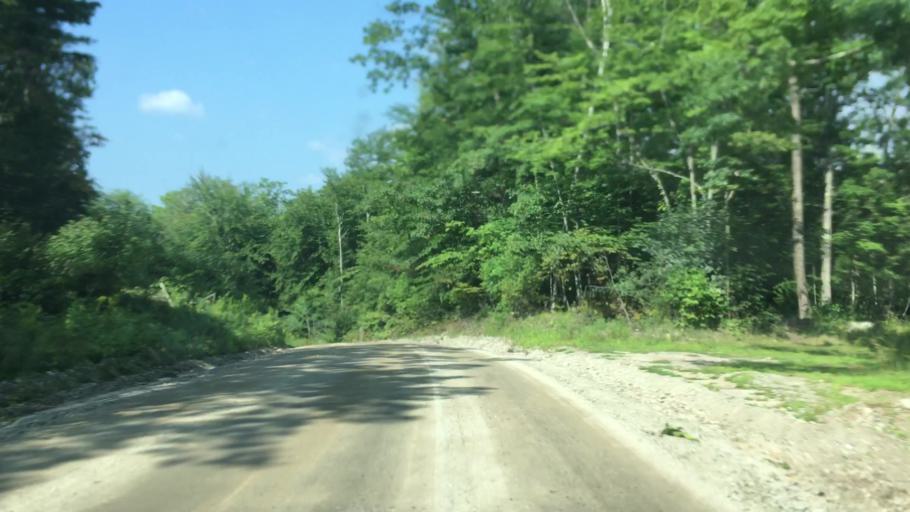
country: US
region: Maine
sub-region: Androscoggin County
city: Poland
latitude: 43.9905
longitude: -70.3722
